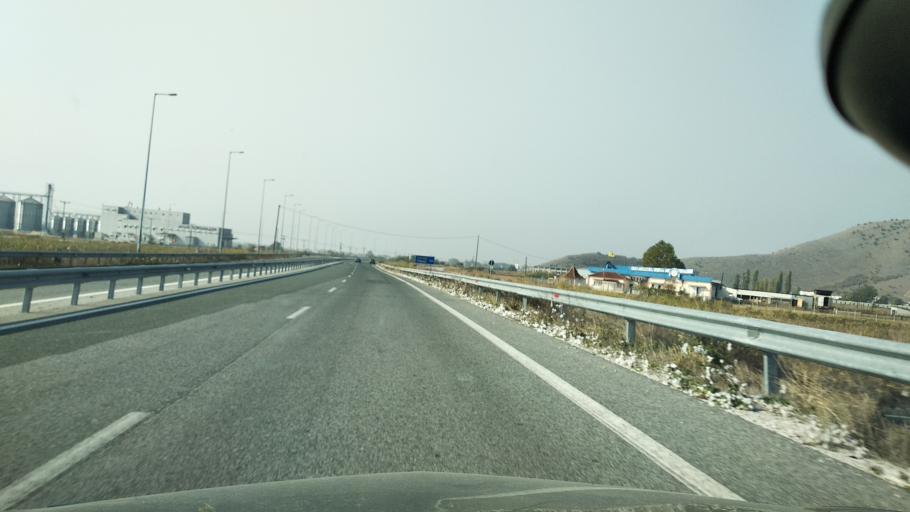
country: GR
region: Thessaly
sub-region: Trikala
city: Oichalia
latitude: 39.5689
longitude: 21.9815
